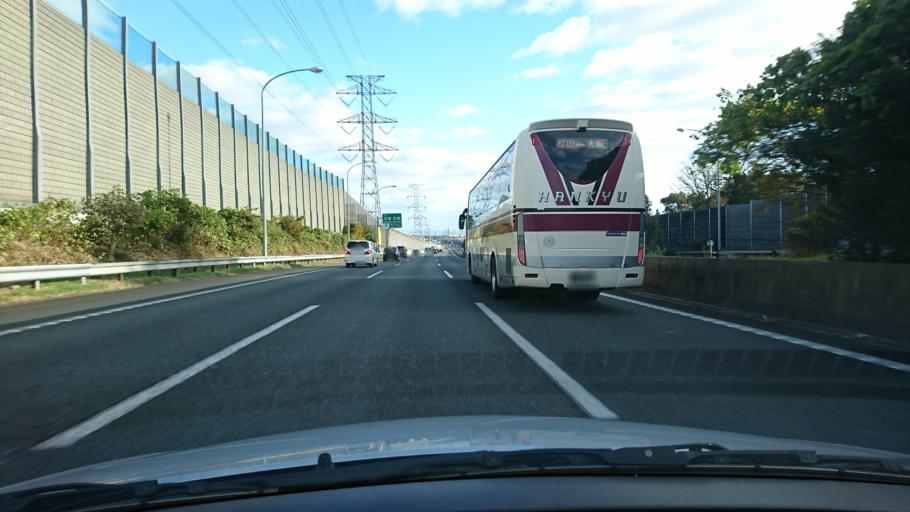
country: JP
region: Hyogo
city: Takarazuka
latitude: 34.8153
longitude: 135.3573
